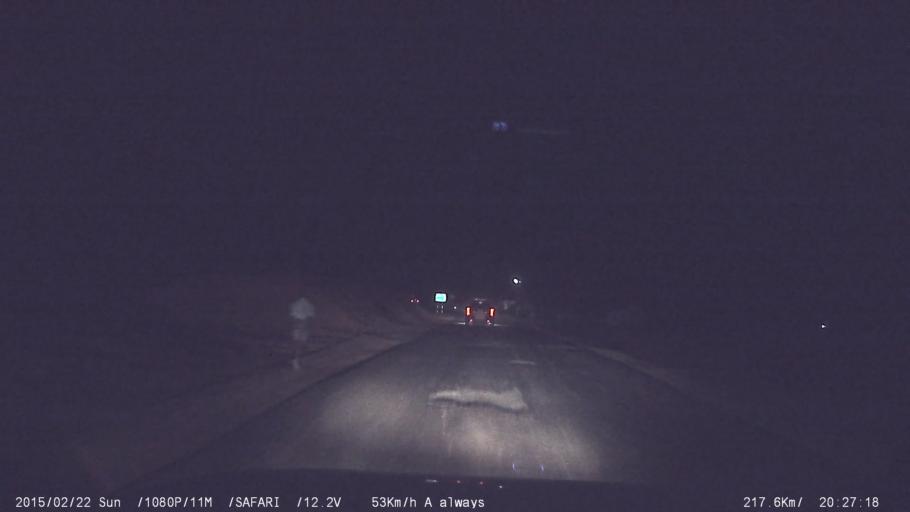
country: IN
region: Tamil Nadu
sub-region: Dindigul
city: Dindigul
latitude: 10.3233
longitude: 77.9118
